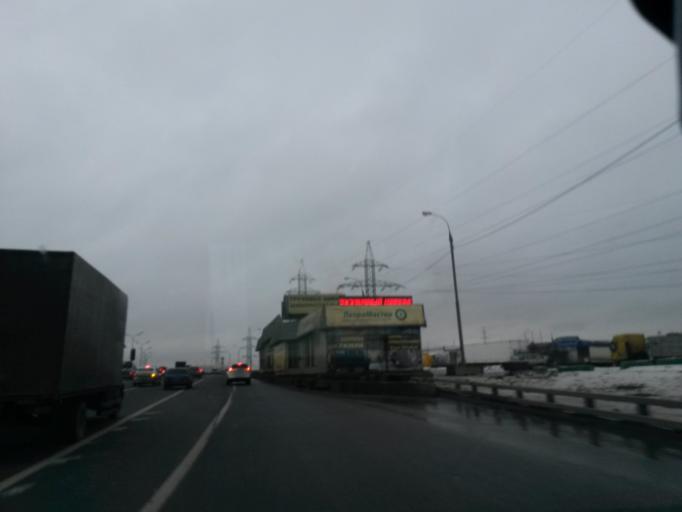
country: RU
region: Moscow
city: Mikhalkovo
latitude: 55.6884
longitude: 37.4149
